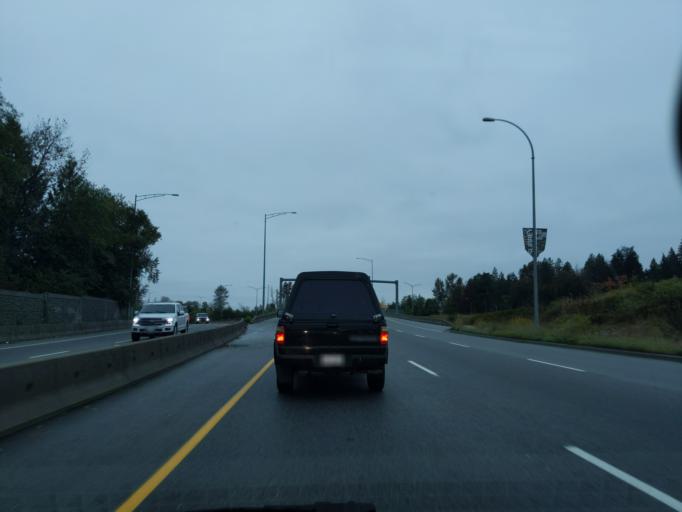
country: CA
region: British Columbia
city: Coquitlam
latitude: 49.1997
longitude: -122.7987
